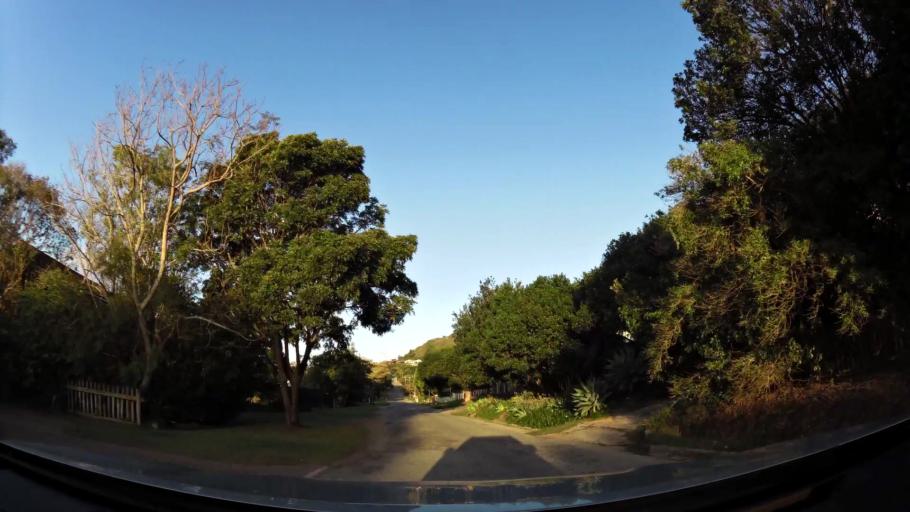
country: ZA
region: Western Cape
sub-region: Eden District Municipality
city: Knysna
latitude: -34.0217
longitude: 22.8065
